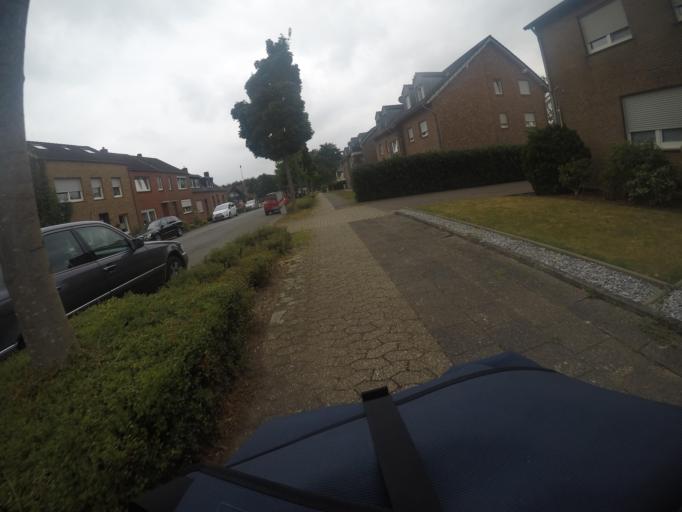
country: DE
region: North Rhine-Westphalia
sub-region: Regierungsbezirk Dusseldorf
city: Kevelaer
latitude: 51.5942
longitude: 6.2360
